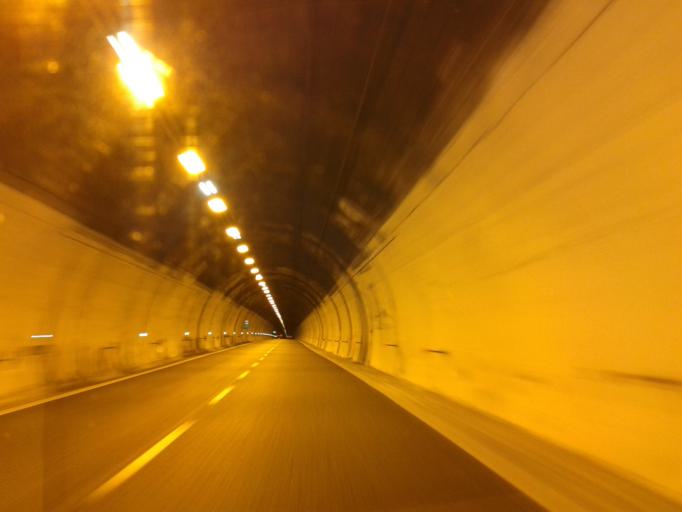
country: IT
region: Liguria
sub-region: Provincia di Genova
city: Cogorno
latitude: 44.3030
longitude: 9.3812
